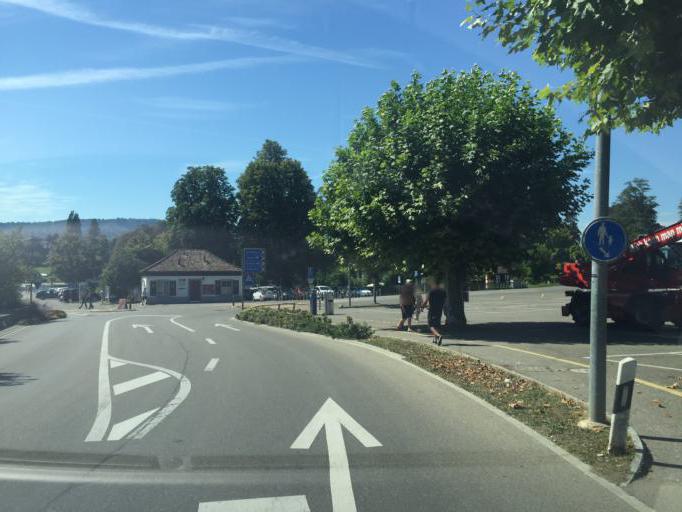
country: CH
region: Schaffhausen
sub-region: Bezirk Stein
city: Stein am Rhein
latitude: 47.6612
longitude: 8.8582
